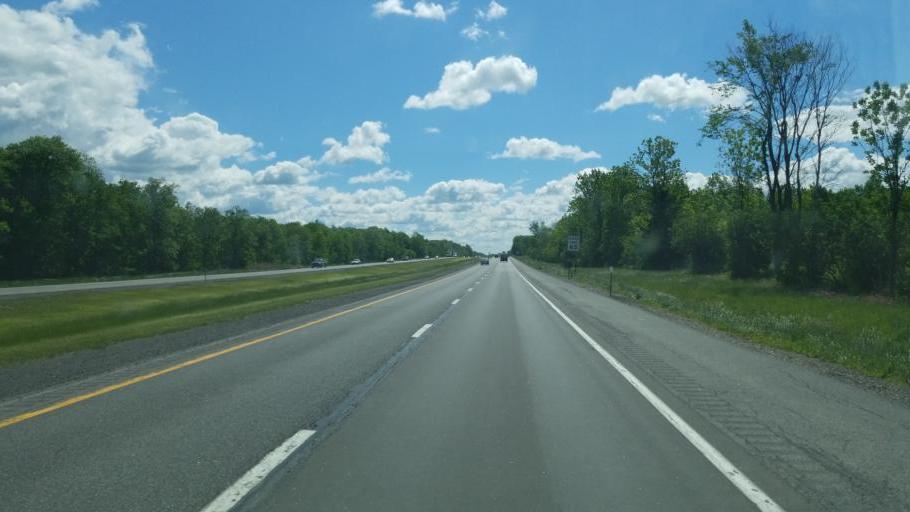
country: US
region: New York
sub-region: Oneida County
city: Rome
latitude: 43.1353
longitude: -75.4770
